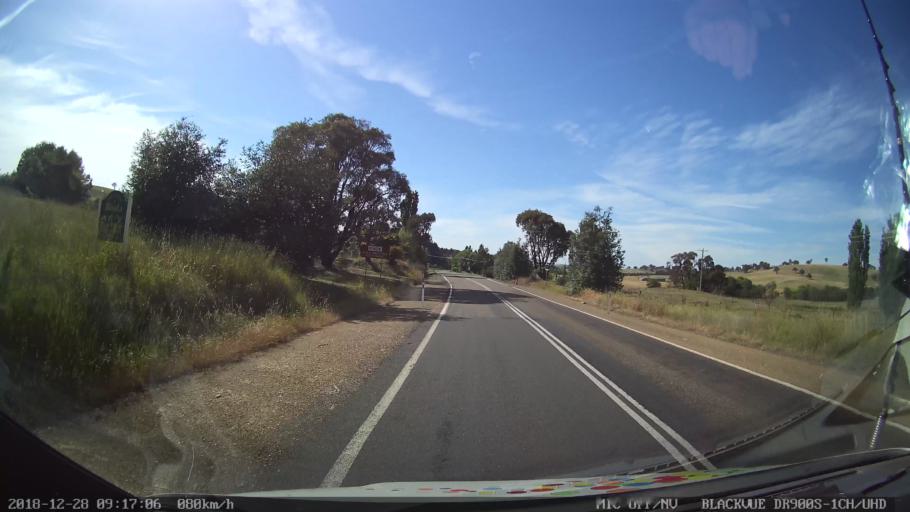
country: AU
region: New South Wales
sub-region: Upper Lachlan Shire
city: Crookwell
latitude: -34.3171
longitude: 149.3587
